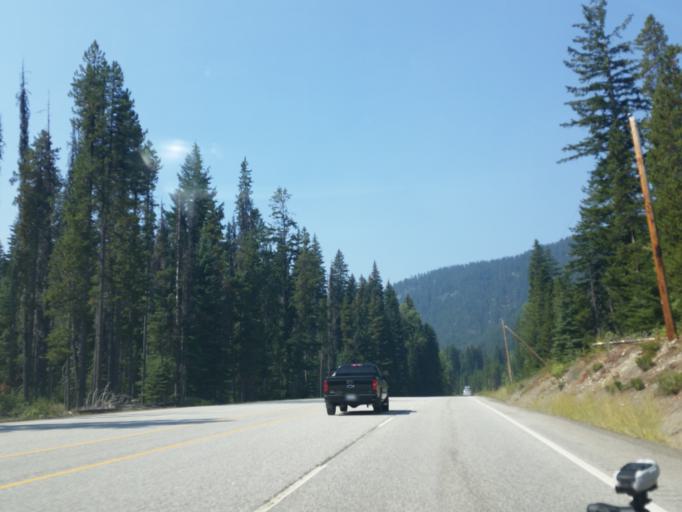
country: CA
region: British Columbia
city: Princeton
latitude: 49.0740
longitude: -120.7066
